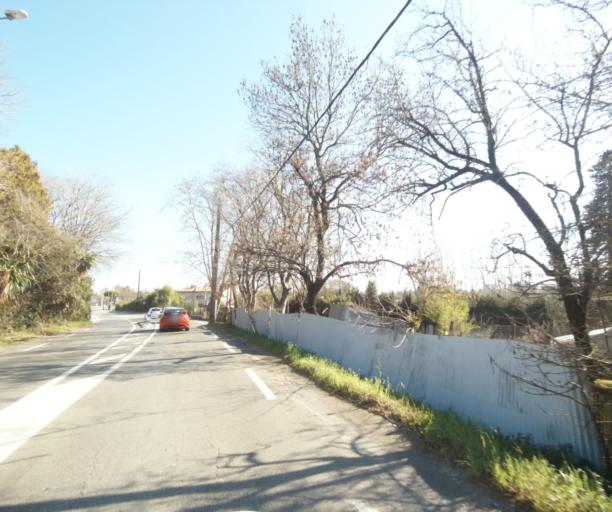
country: FR
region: Provence-Alpes-Cote d'Azur
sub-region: Departement des Alpes-Maritimes
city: Biot
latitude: 43.6154
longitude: 7.1177
